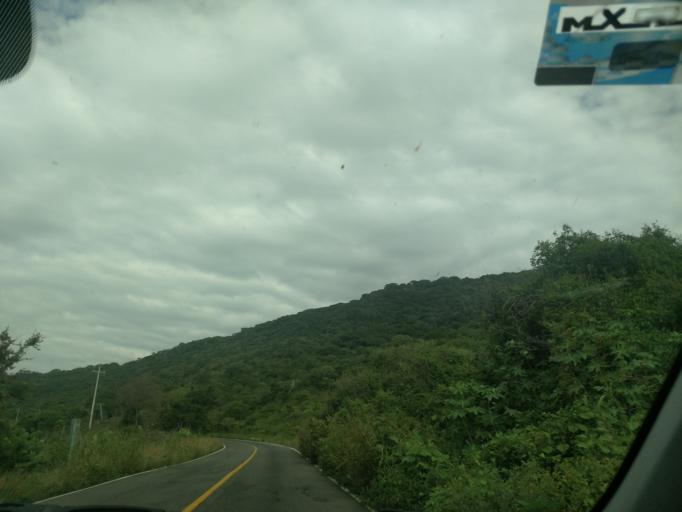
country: MX
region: Jalisco
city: Ameca
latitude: 20.5277
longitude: -104.2120
